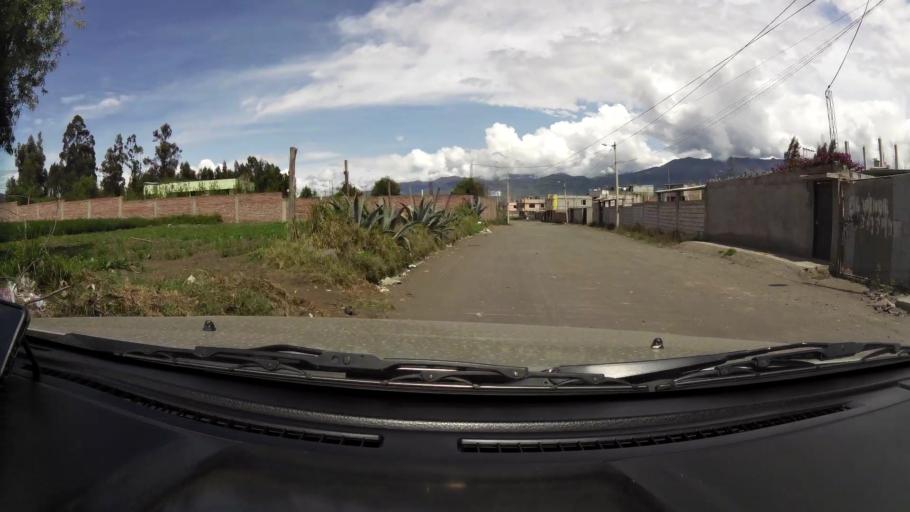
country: EC
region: Chimborazo
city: Riobamba
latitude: -1.6560
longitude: -78.6375
